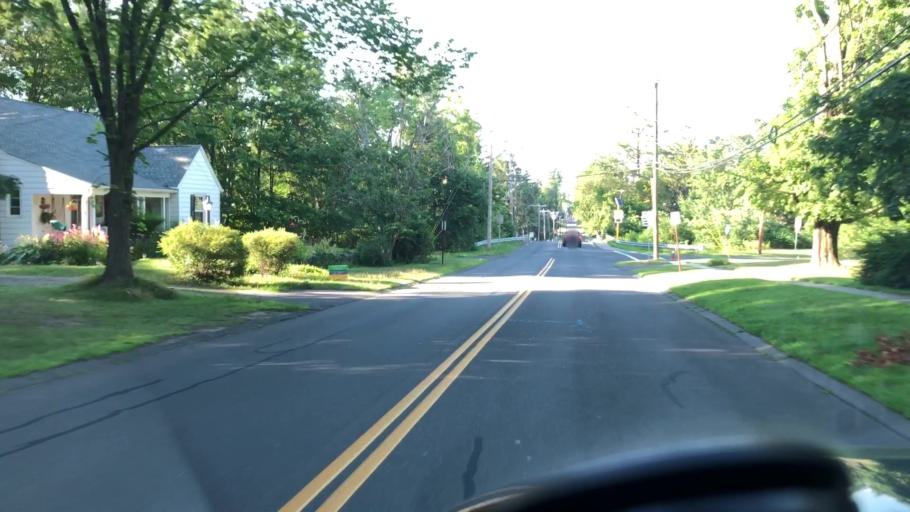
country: US
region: Massachusetts
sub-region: Hampshire County
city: Easthampton
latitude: 42.2613
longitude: -72.6776
